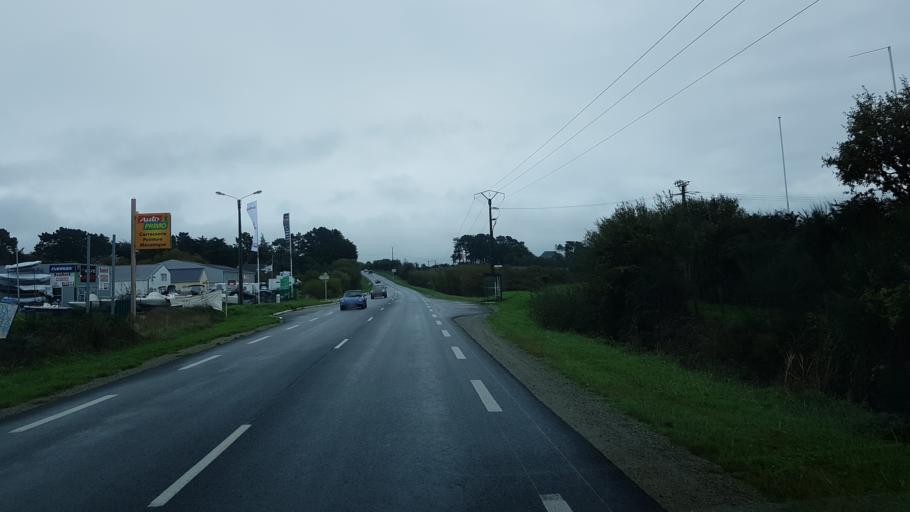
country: FR
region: Brittany
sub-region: Departement du Morbihan
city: Saint-Gildas-de-Rhuys
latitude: 47.5339
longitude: -2.8546
